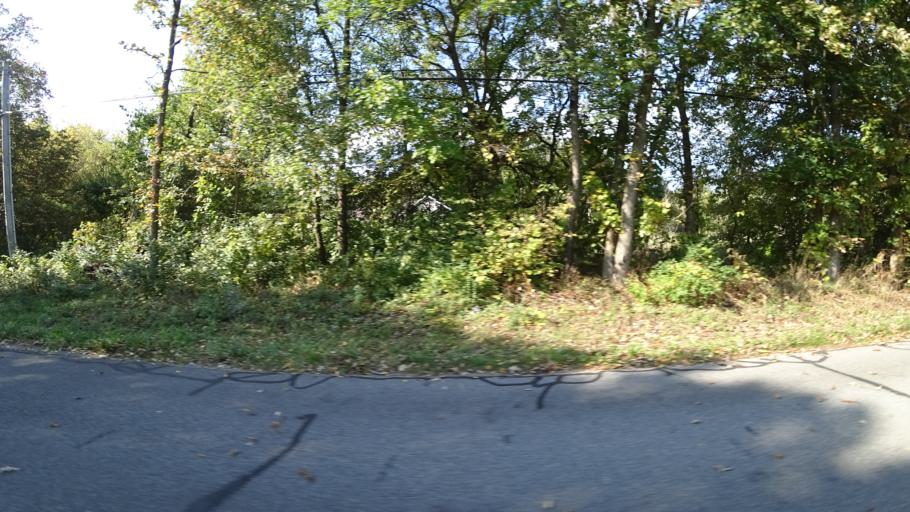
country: US
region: Michigan
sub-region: Saint Joseph County
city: Three Rivers
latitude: 41.9266
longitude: -85.6358
